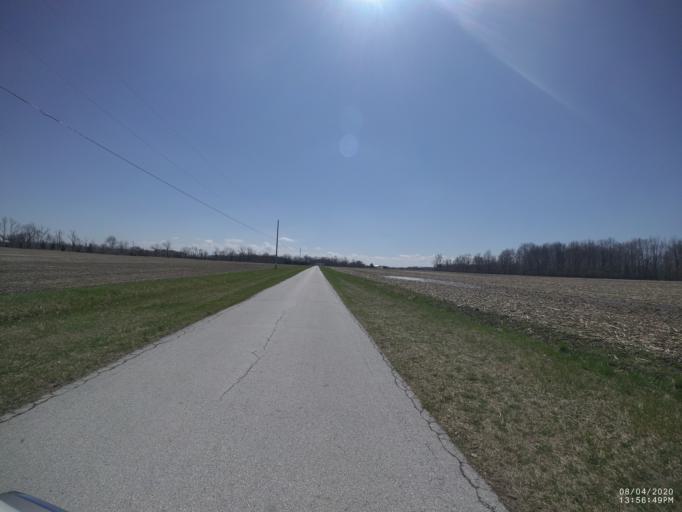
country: US
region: Ohio
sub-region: Sandusky County
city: Gibsonburg
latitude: 41.3108
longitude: -83.2834
